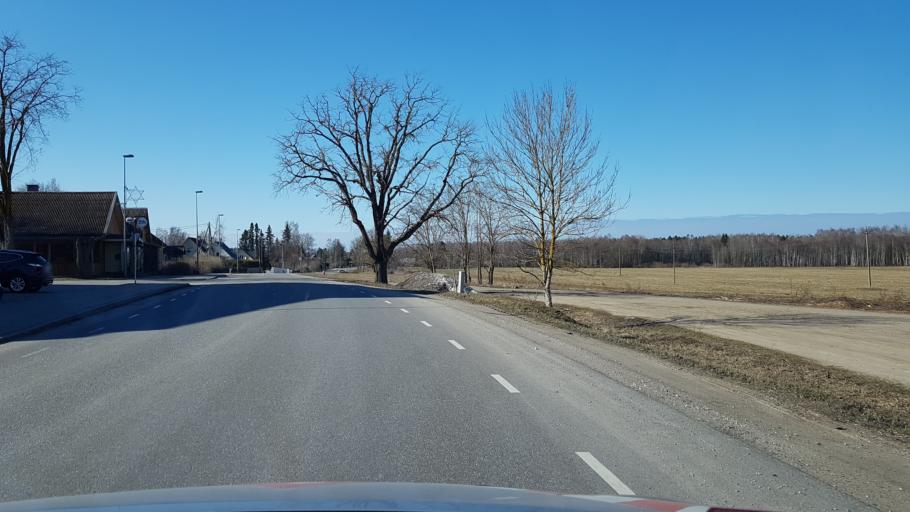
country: EE
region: Laeaene-Virumaa
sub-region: Haljala vald
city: Haljala
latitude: 59.4338
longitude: 26.2676
